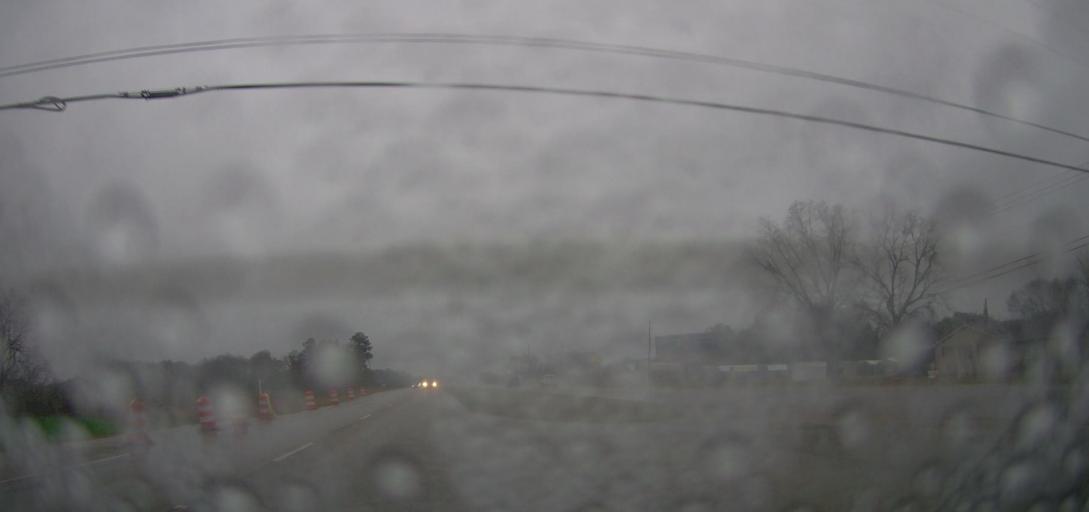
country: US
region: Alabama
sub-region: Autauga County
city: Prattville
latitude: 32.4362
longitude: -86.4228
